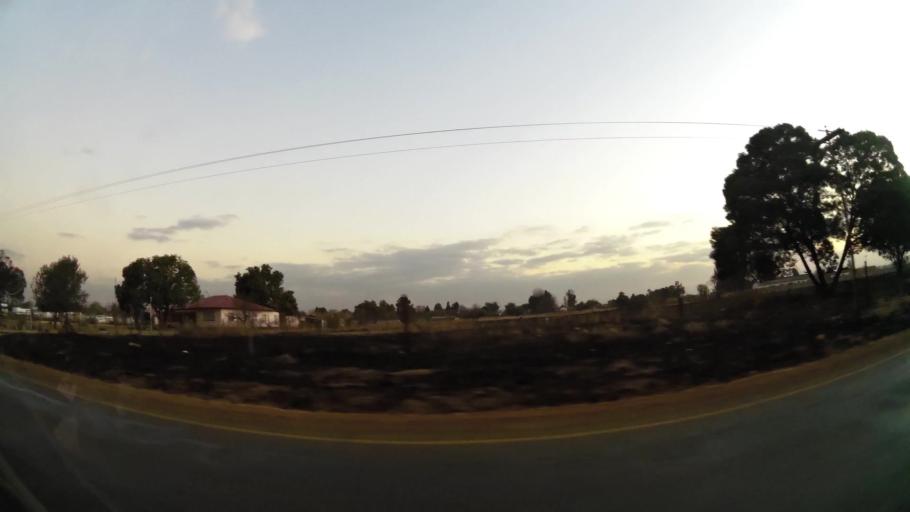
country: ZA
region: Gauteng
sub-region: West Rand District Municipality
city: Randfontein
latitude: -26.0881
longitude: 27.6684
